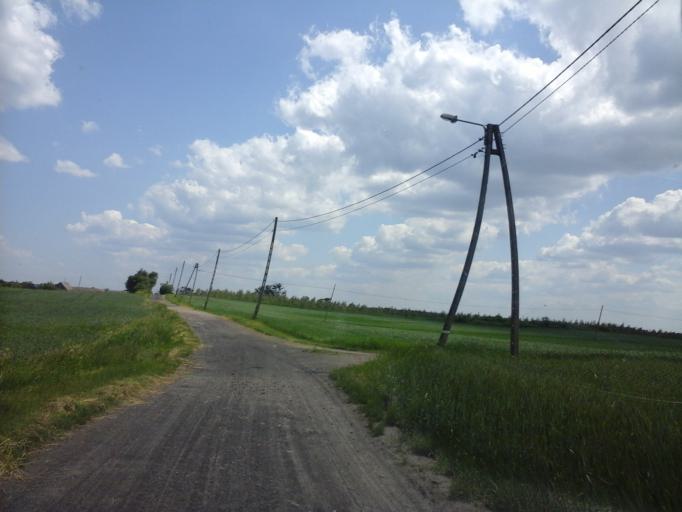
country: PL
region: West Pomeranian Voivodeship
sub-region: Powiat choszczenski
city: Bierzwnik
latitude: 53.0344
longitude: 15.7055
